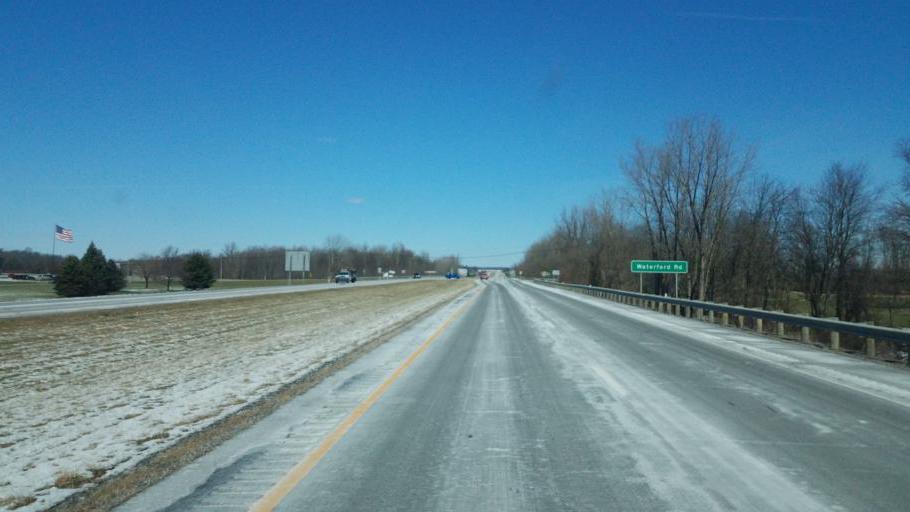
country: US
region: Ohio
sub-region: Knox County
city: Fredericktown
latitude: 40.4894
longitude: -82.5583
